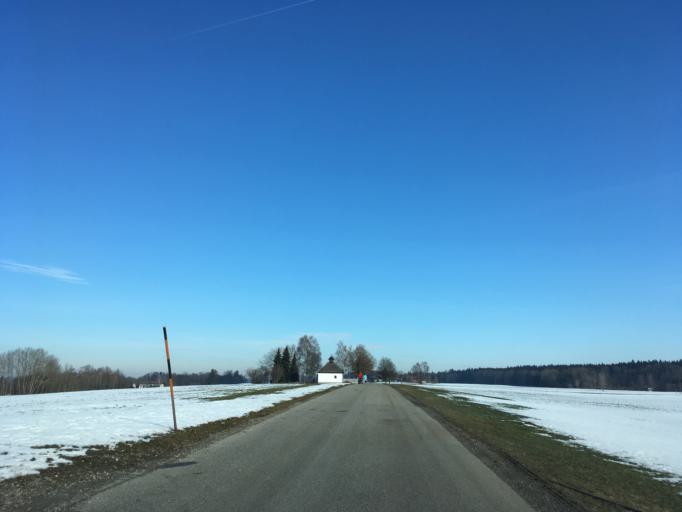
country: DE
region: Bavaria
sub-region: Upper Bavaria
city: Schechen
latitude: 47.9054
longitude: 12.1477
